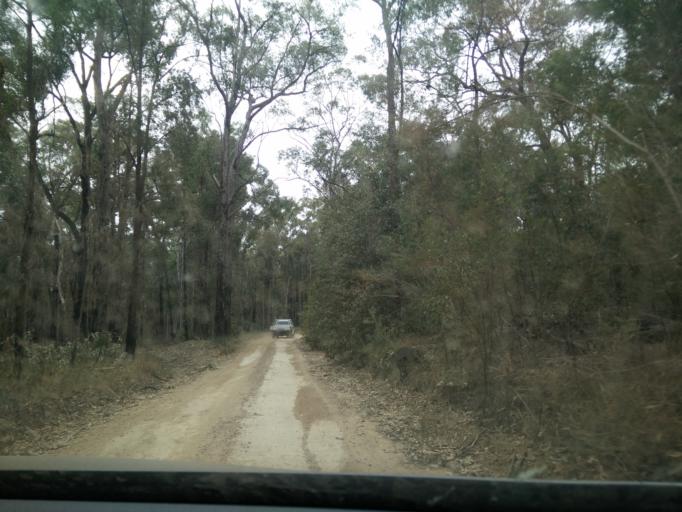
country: AU
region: New South Wales
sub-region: Penrith Municipality
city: Mulgoa
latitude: -33.8331
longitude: 150.5787
